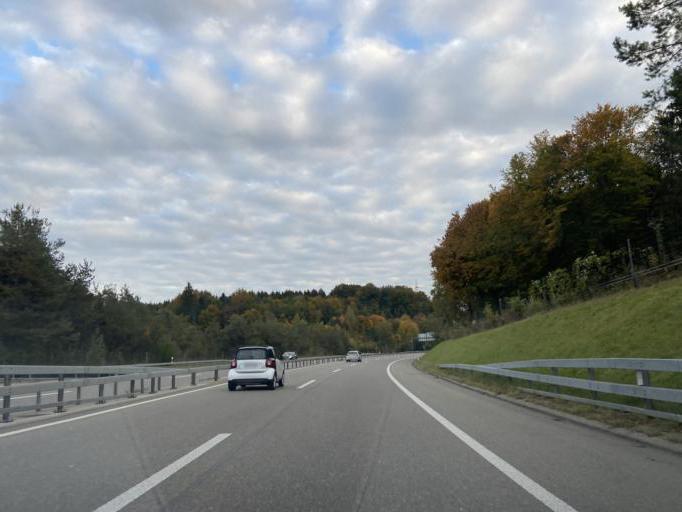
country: CH
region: Zurich
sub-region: Bezirk Pfaeffikon
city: Effretikon / Watt
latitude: 47.4412
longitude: 8.6959
